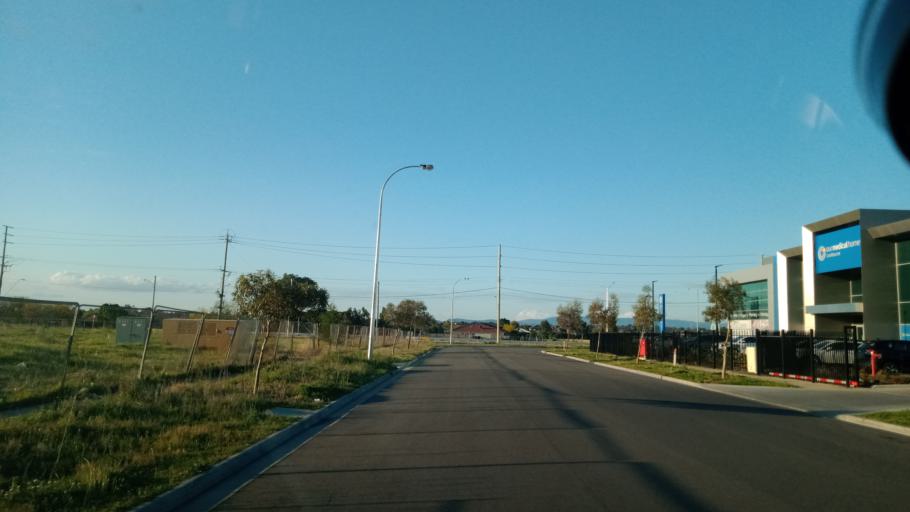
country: AU
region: Victoria
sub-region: Casey
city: Lynbrook
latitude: -38.0796
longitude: 145.2458
